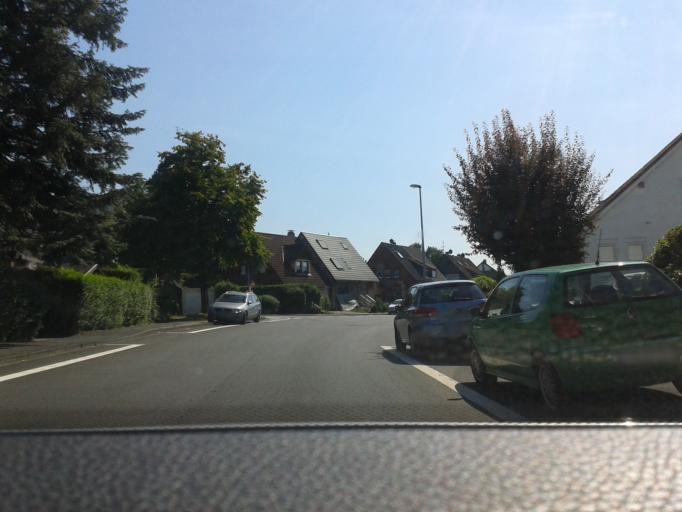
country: DE
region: North Rhine-Westphalia
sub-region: Regierungsbezirk Dusseldorf
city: Muelheim (Ruhr)
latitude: 51.3941
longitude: 6.8575
